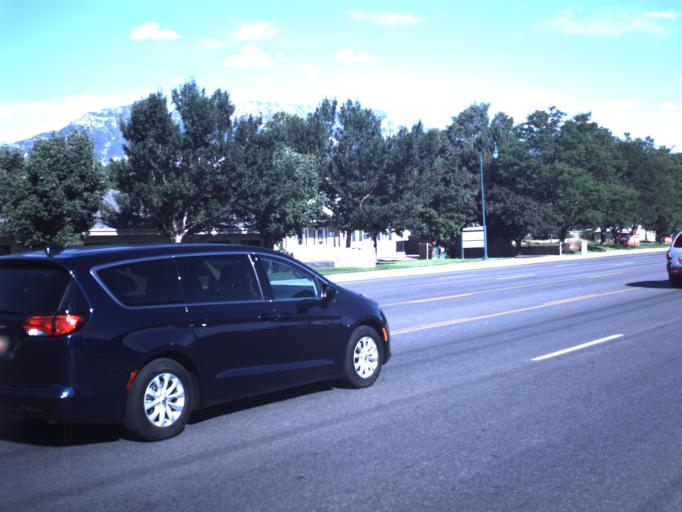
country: US
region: Utah
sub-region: Utah County
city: Lindon
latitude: 40.3302
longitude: -111.7107
